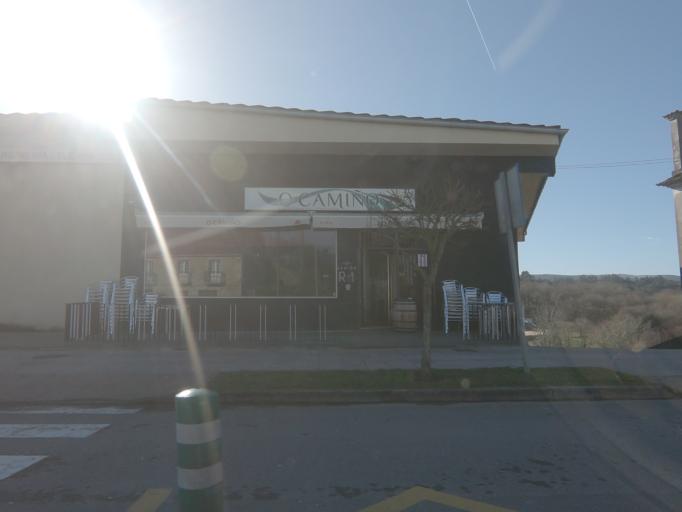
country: ES
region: Galicia
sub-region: Provincia de Pontevedra
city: Silleda
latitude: 42.6993
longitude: -8.2512
